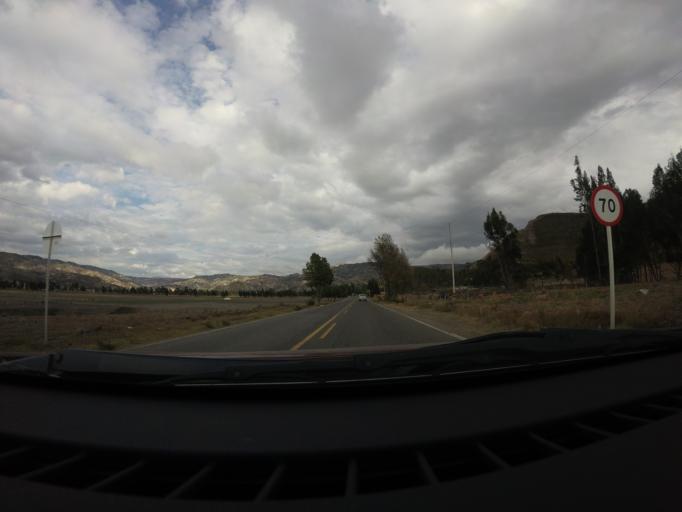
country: CO
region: Boyaca
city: Cucaita
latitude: 5.5413
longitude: -73.4721
